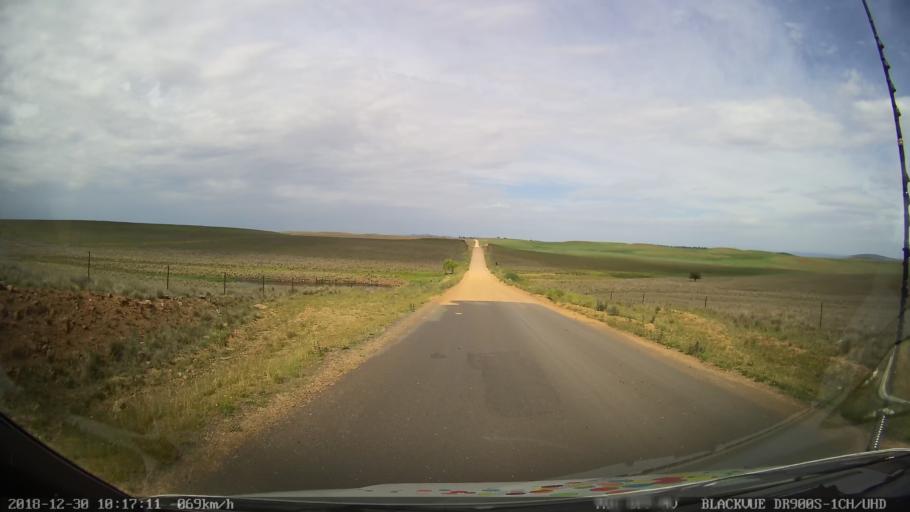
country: AU
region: New South Wales
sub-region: Snowy River
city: Berridale
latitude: -36.5478
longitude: 149.0243
